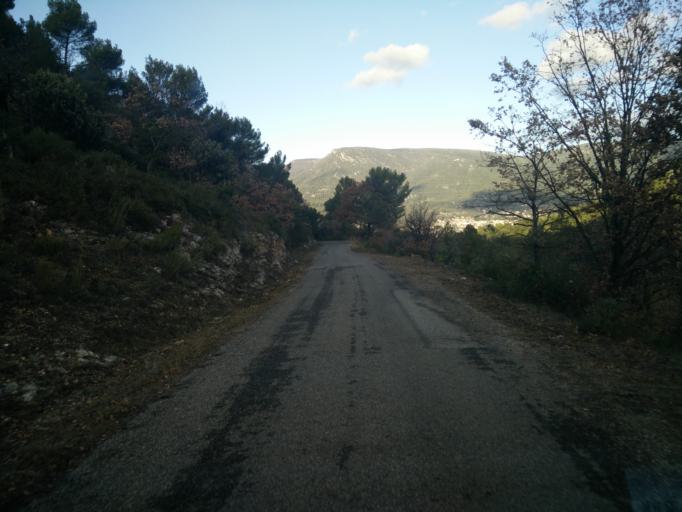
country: FR
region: Provence-Alpes-Cote d'Azur
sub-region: Departement du Var
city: Signes
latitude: 43.2723
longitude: 5.8465
